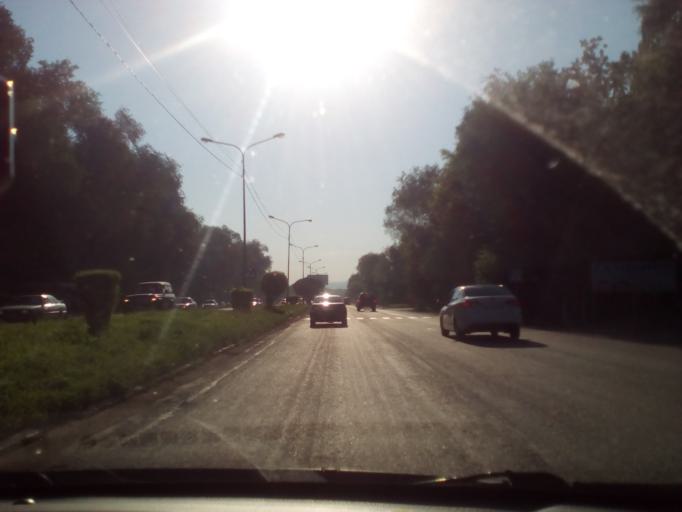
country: KZ
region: Almaty Oblysy
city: Burunday
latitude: 43.2138
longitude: 76.6822
